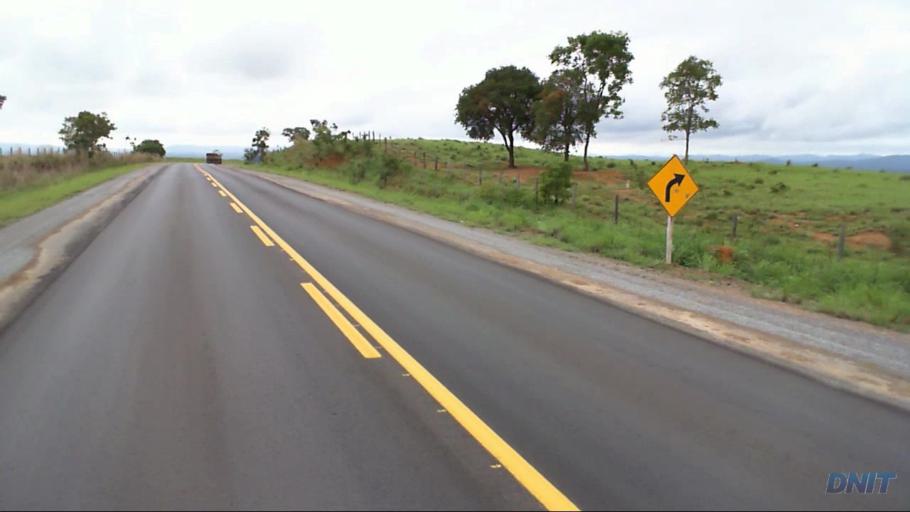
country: BR
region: Goias
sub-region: Padre Bernardo
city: Padre Bernardo
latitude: -15.2197
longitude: -48.5184
